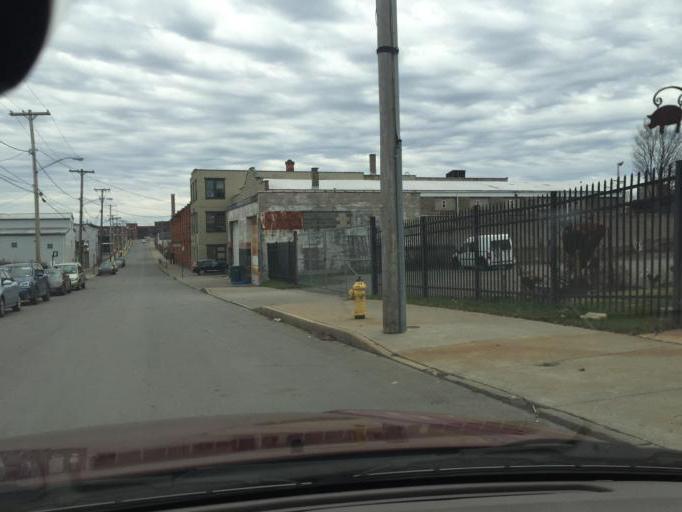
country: US
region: New York
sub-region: Monroe County
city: Rochester
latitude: 43.1641
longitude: -77.5881
